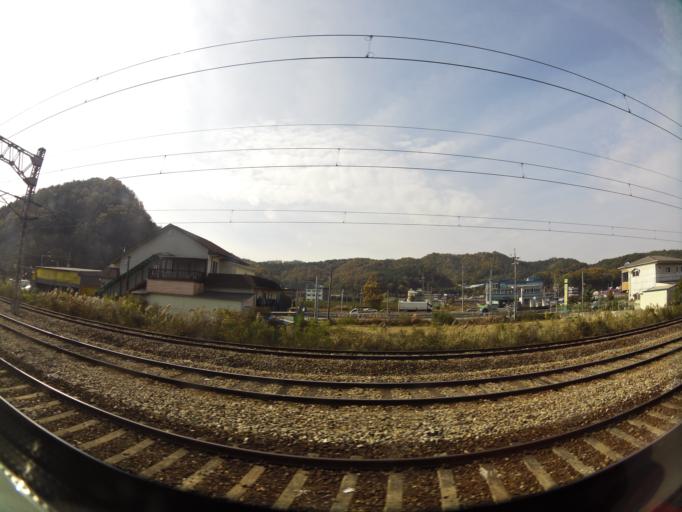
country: KR
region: Chungcheongbuk-do
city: Cheongju-si
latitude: 36.6267
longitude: 127.2905
